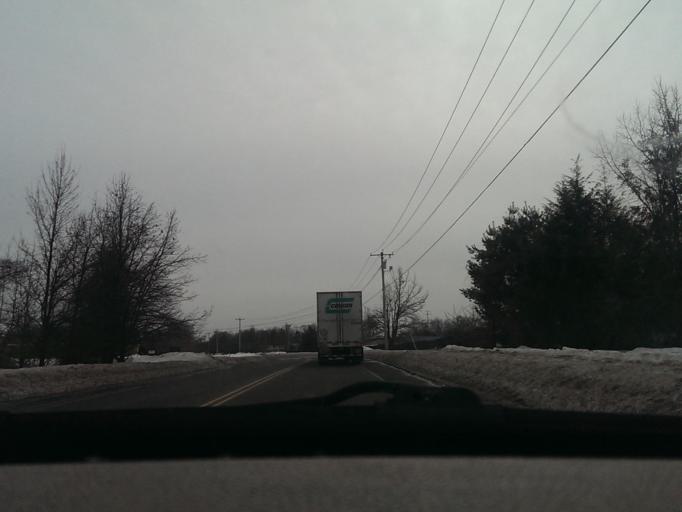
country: US
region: Massachusetts
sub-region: Hampden County
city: East Longmeadow
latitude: 42.0493
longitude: -72.5325
